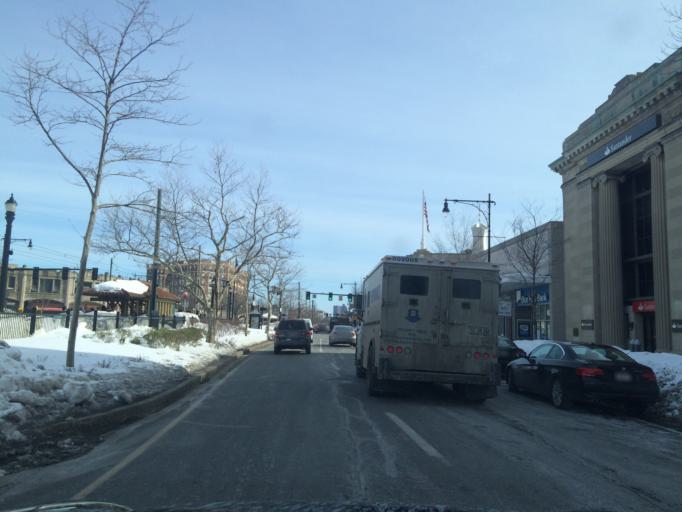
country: US
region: Massachusetts
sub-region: Norfolk County
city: Brookline
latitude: 42.3416
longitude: -71.1223
